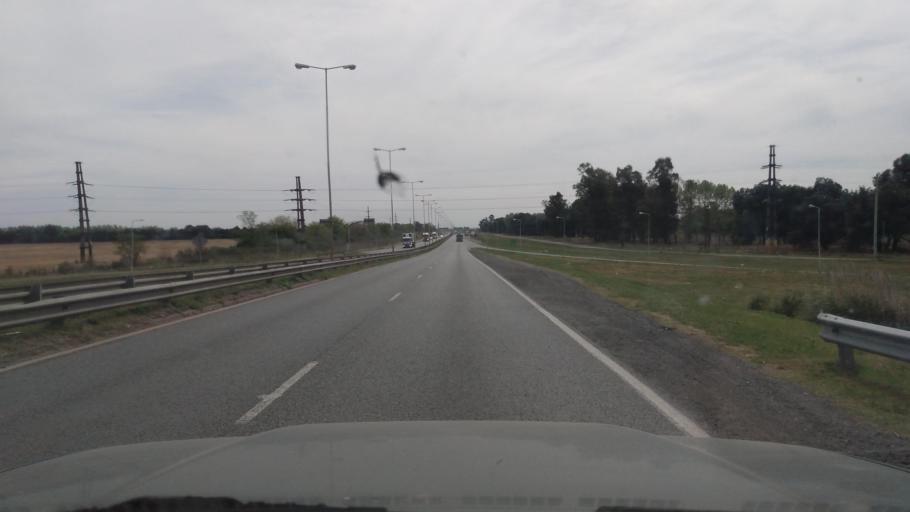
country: AR
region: Buenos Aires
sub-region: Partido de Lujan
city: Lujan
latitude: -34.5724
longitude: -59.0370
